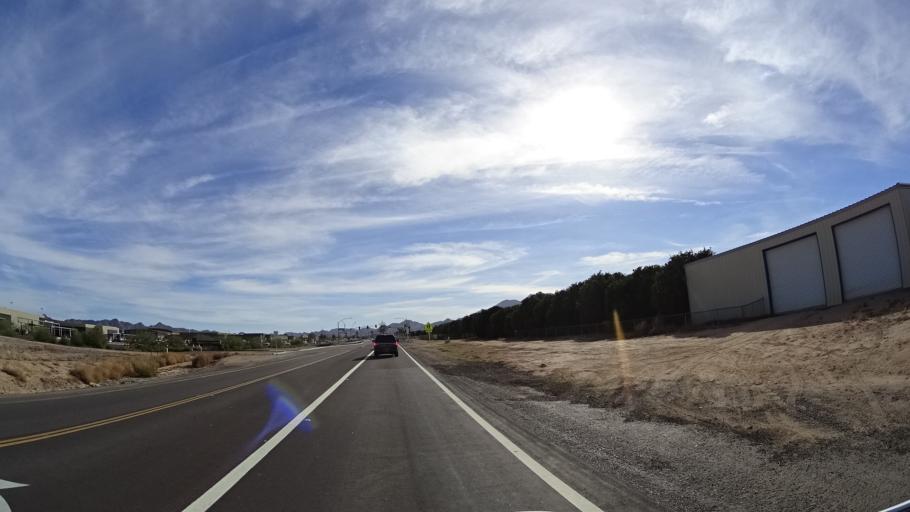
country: US
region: Arizona
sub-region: Maricopa County
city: Queen Creek
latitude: 33.2251
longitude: -111.6859
